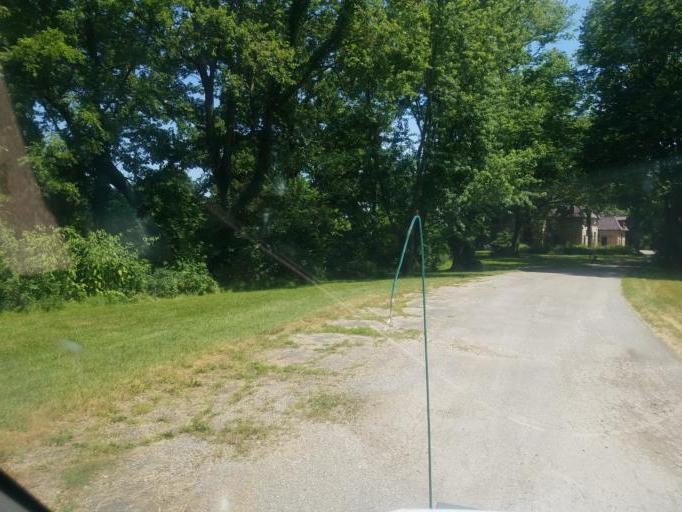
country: US
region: Ohio
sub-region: Logan County
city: West Liberty
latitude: 40.2502
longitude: -83.7278
